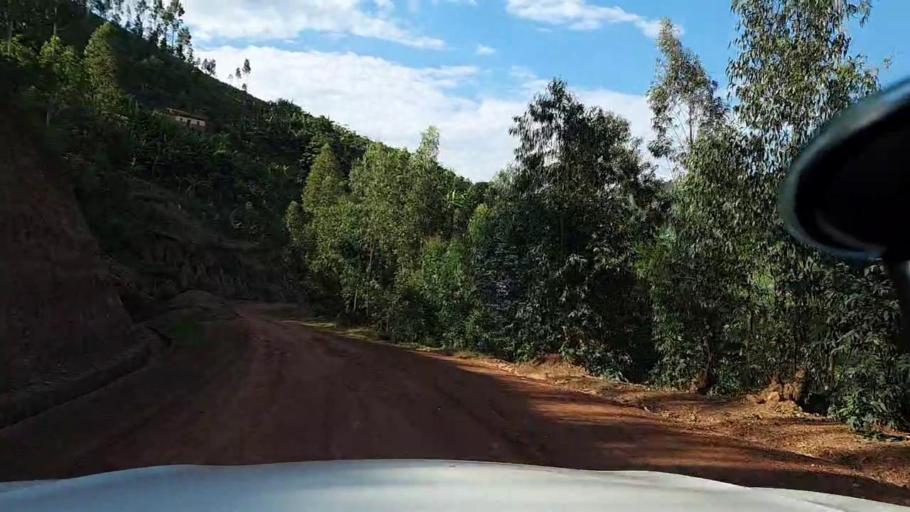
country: RW
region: Kigali
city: Kigali
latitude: -1.8456
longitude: 29.8656
